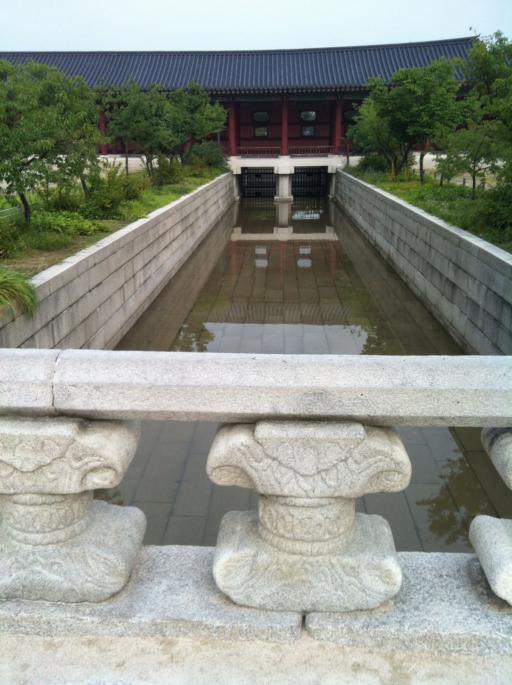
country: KR
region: Seoul
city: Seoul
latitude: 37.5773
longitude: 126.9769
